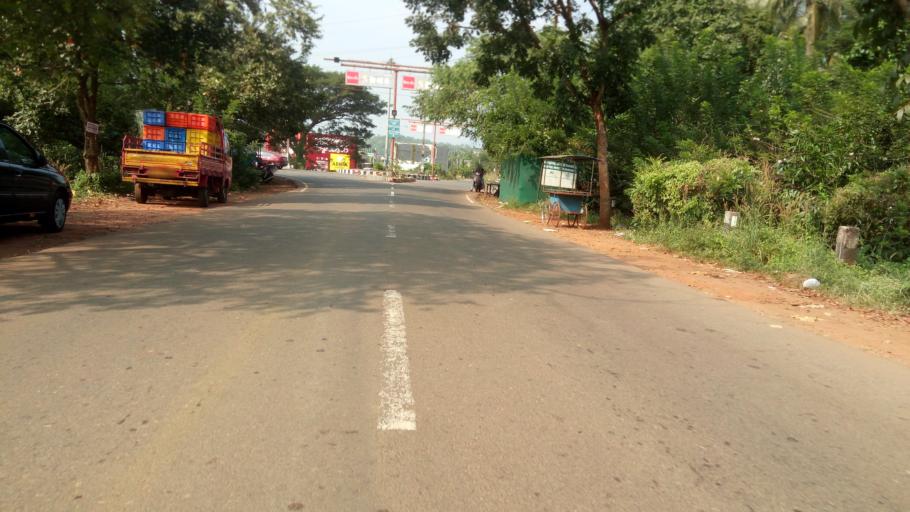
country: IN
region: Kerala
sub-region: Malappuram
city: Malappuram
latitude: 11.0031
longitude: 76.0143
